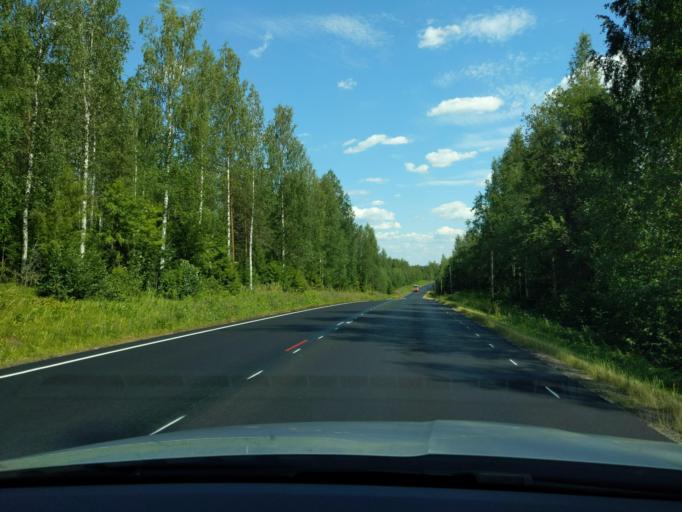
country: FI
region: Paijanne Tavastia
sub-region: Lahti
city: Nastola
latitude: 61.0863
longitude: 25.8516
